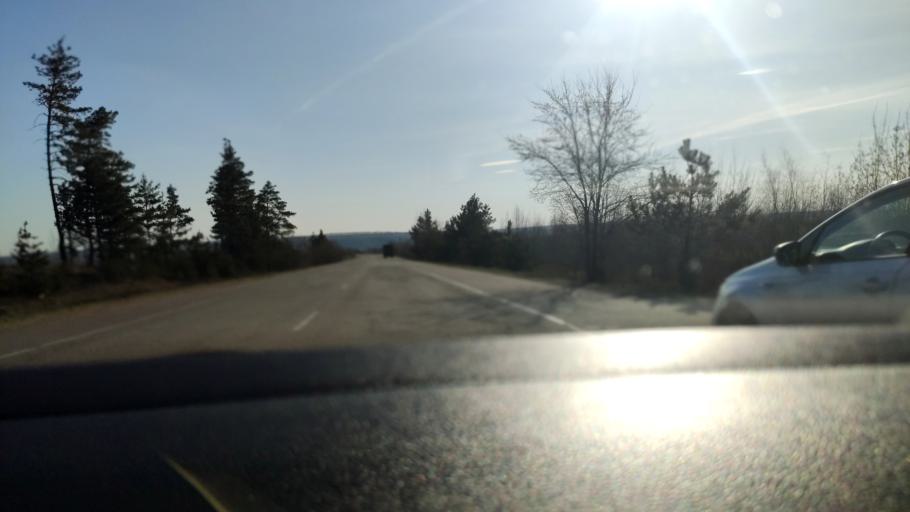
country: RU
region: Voronezj
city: Kolodeznyy
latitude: 51.3600
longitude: 39.1839
